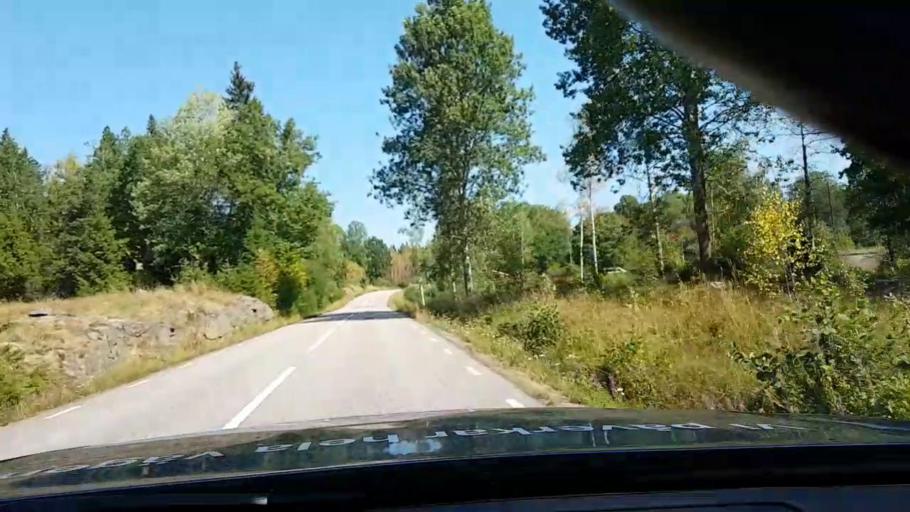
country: SE
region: Kalmar
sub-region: Hultsfreds Kommun
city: Virserum
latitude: 57.1293
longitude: 15.6565
